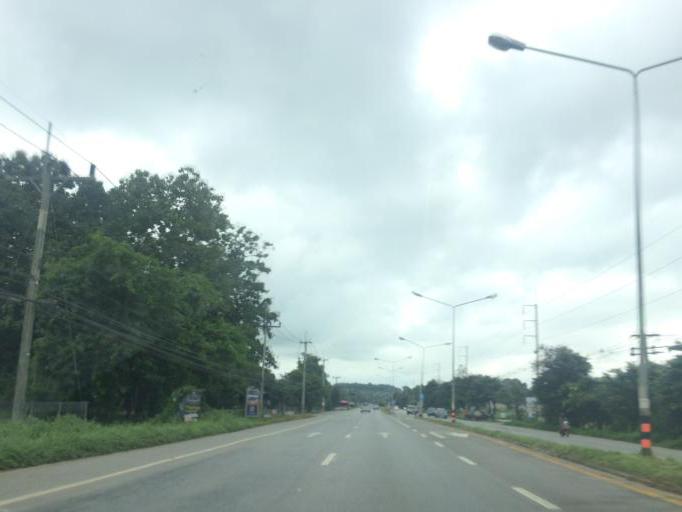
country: TH
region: Chiang Rai
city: Mae Chan
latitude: 20.1028
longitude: 99.8739
